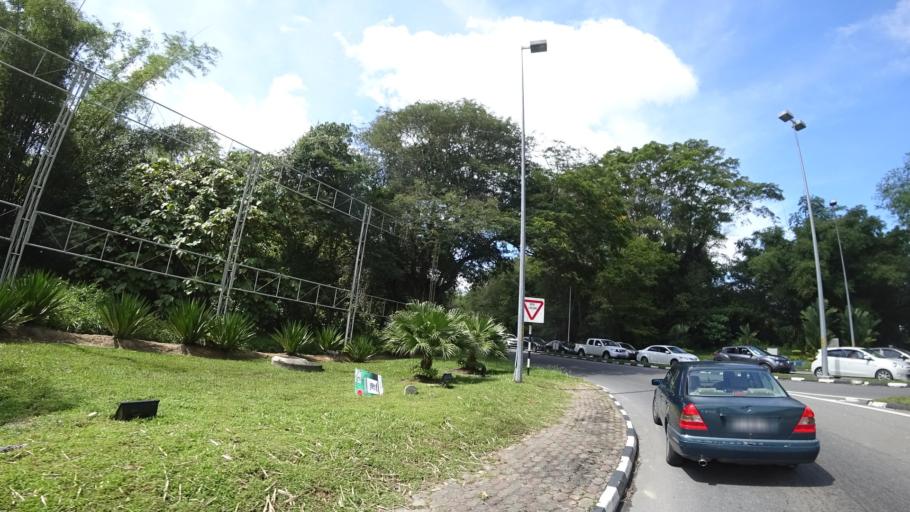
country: BN
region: Brunei and Muara
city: Bandar Seri Begawan
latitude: 4.8635
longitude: 114.9013
